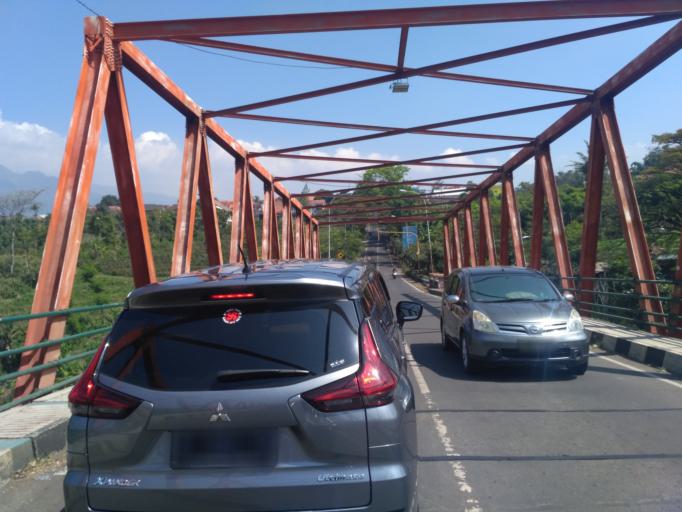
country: ID
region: East Java
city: Batu
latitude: -7.8644
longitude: 112.5483
